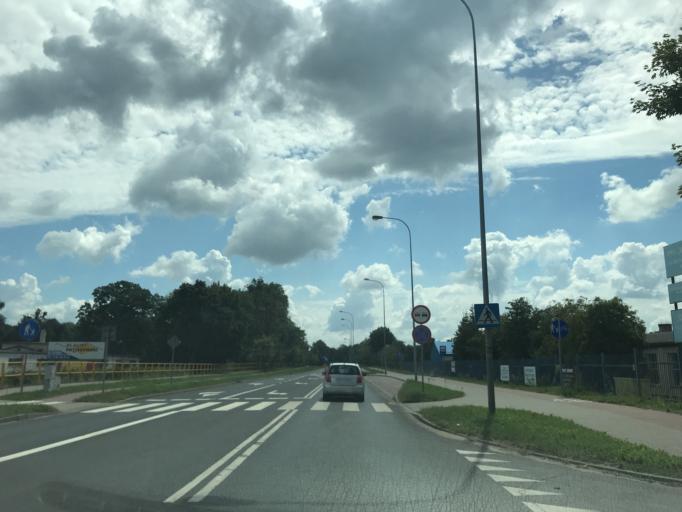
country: PL
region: Warmian-Masurian Voivodeship
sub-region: Powiat ostrodzki
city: Ostroda
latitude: 53.6888
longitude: 19.9846
